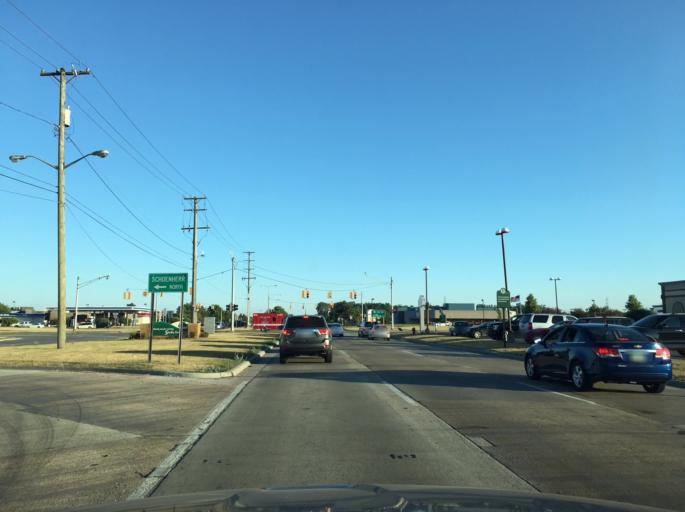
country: US
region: Michigan
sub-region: Macomb County
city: Utica
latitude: 42.6282
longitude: -82.9933
